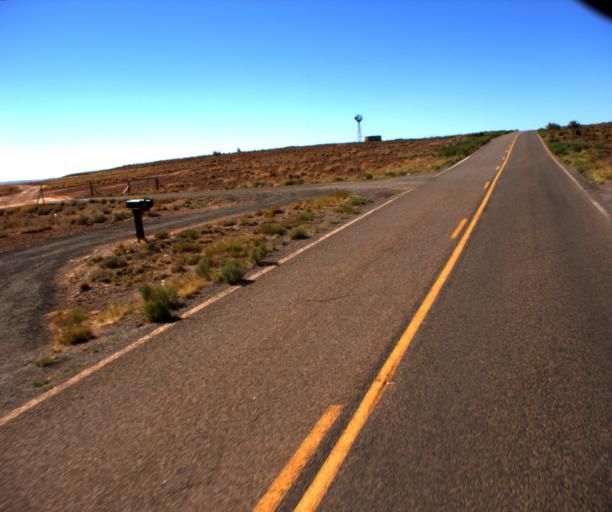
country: US
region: Arizona
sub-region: Coconino County
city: LeChee
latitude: 35.2444
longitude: -110.9606
